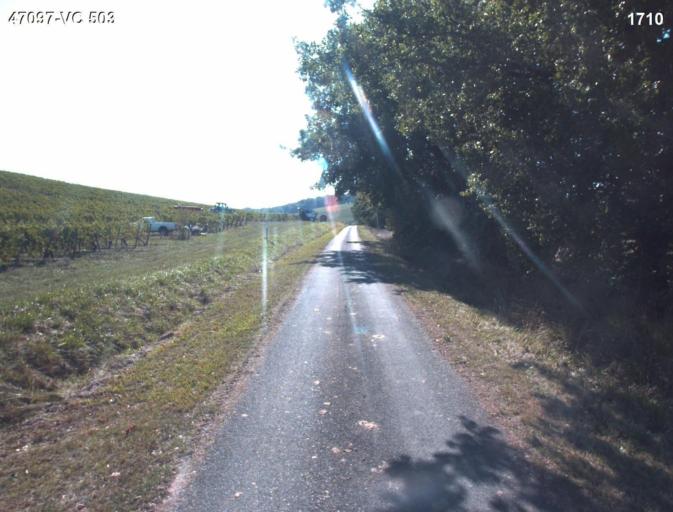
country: FR
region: Aquitaine
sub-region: Departement du Lot-et-Garonne
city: Port-Sainte-Marie
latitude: 44.2067
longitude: 0.3712
